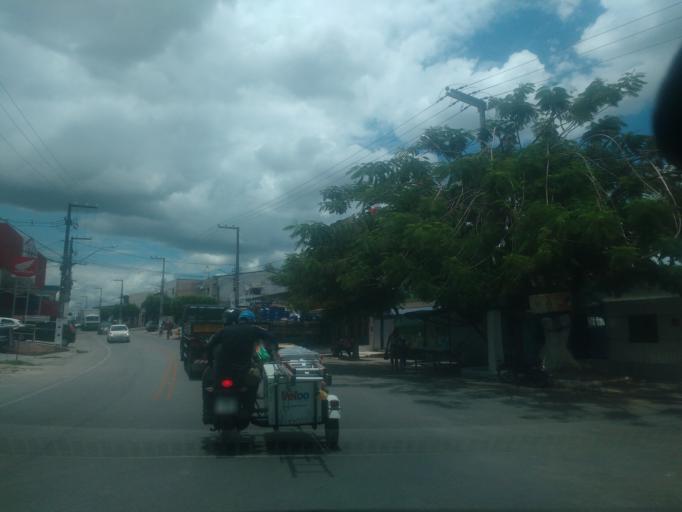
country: BR
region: Alagoas
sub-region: Uniao Dos Palmares
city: Uniao dos Palmares
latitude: -9.1566
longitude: -36.0264
